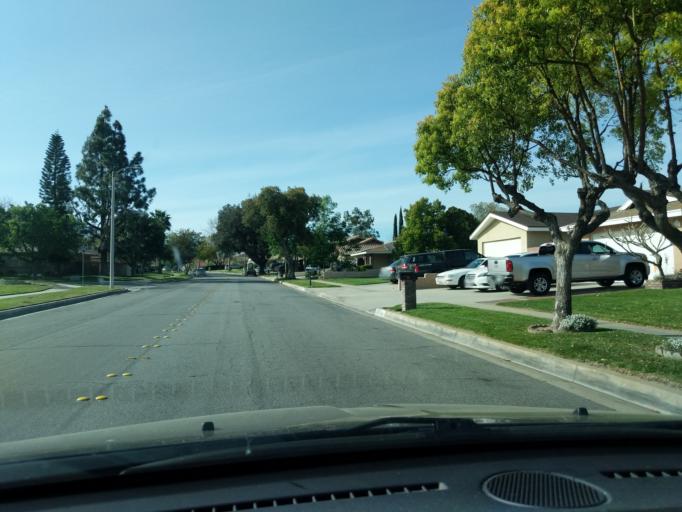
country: US
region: California
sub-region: San Bernardino County
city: Muscoy
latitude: 34.1397
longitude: -117.3673
